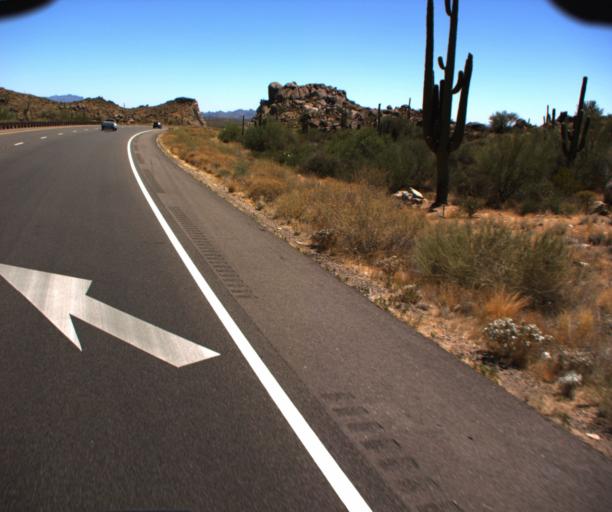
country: US
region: Arizona
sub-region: Maricopa County
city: Rio Verde
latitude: 33.6983
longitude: -111.5021
